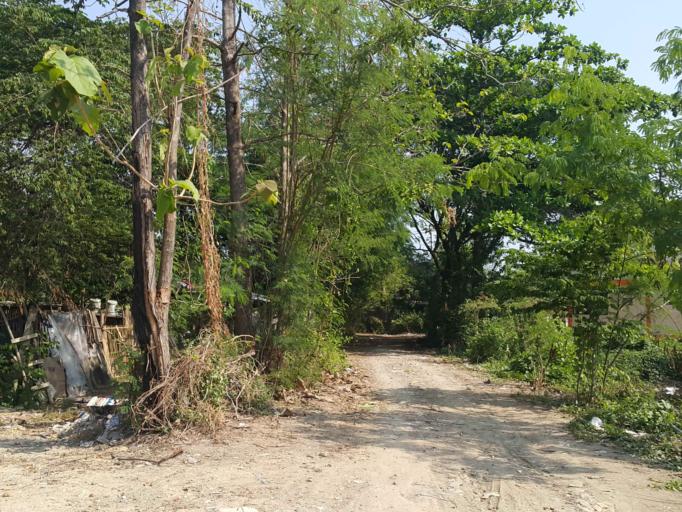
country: TH
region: Chiang Mai
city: San Kamphaeng
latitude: 18.7629
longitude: 99.0729
